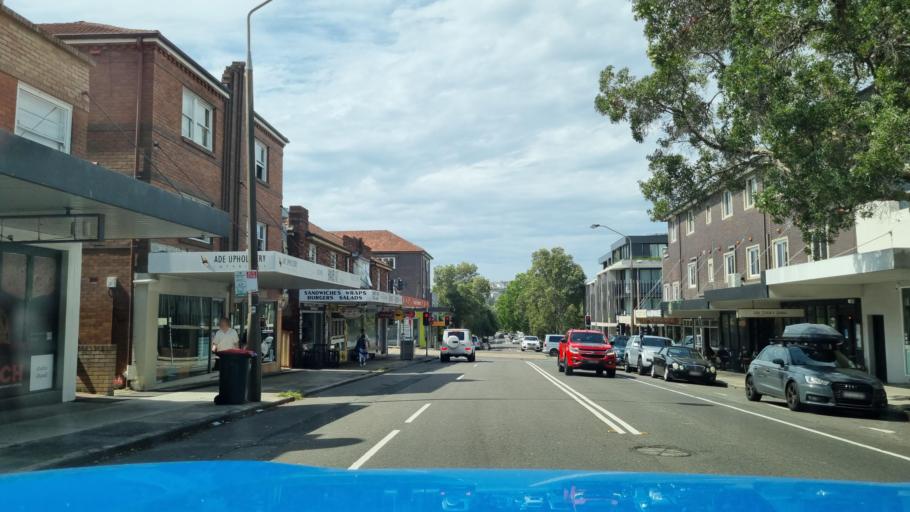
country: AU
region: New South Wales
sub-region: Waverley
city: Bondi Beach
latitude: -33.8879
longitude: 151.2715
